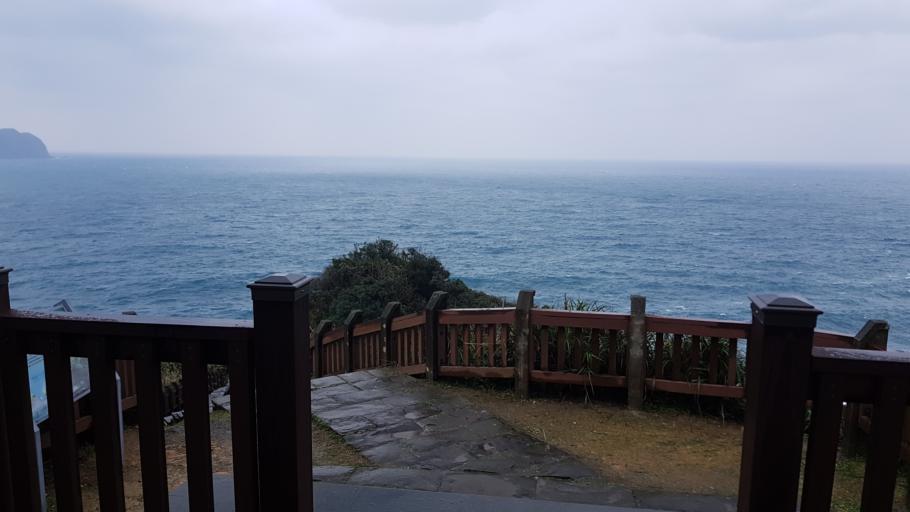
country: TW
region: Taiwan
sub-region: Keelung
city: Keelung
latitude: 25.1461
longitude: 121.7968
